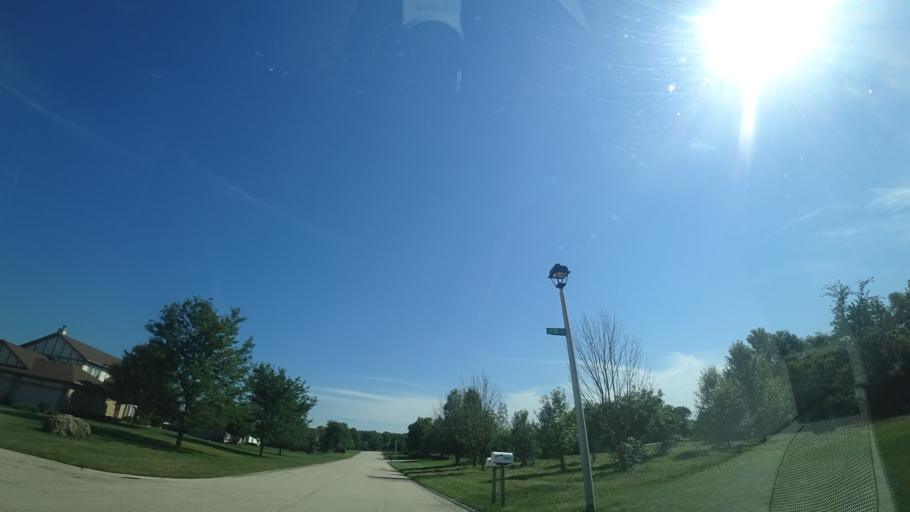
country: US
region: Illinois
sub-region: Will County
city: Homer Glen
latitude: 41.5605
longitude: -87.9180
